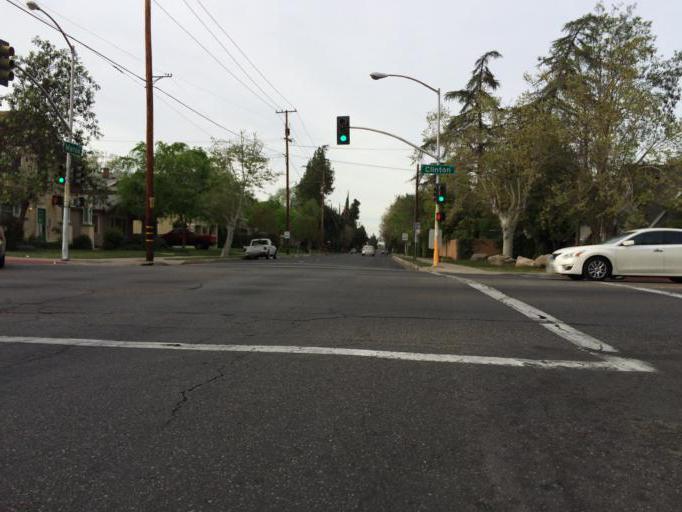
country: US
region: California
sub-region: Fresno County
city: Fresno
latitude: 36.7720
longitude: -119.7995
